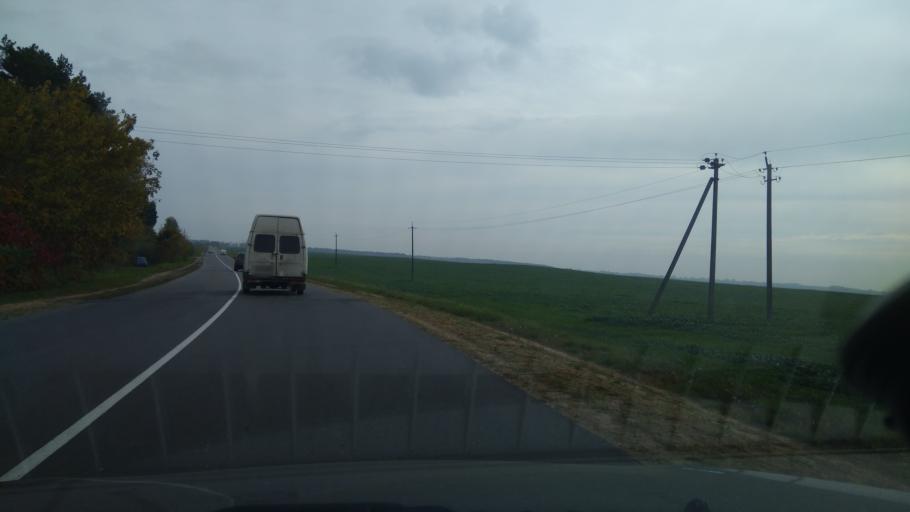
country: BY
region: Minsk
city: Rudzyensk
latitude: 53.6102
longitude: 27.8018
